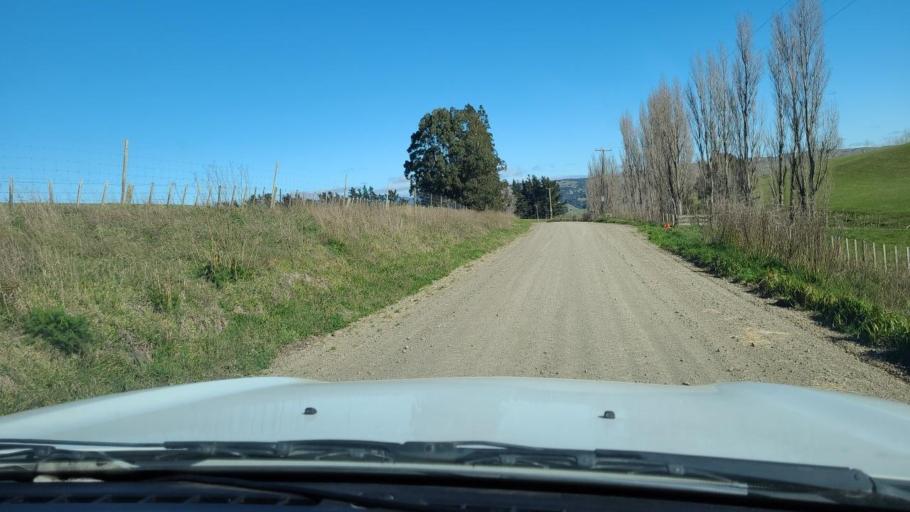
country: NZ
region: Hawke's Bay
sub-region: Napier City
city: Taradale
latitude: -39.4936
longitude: 176.4867
